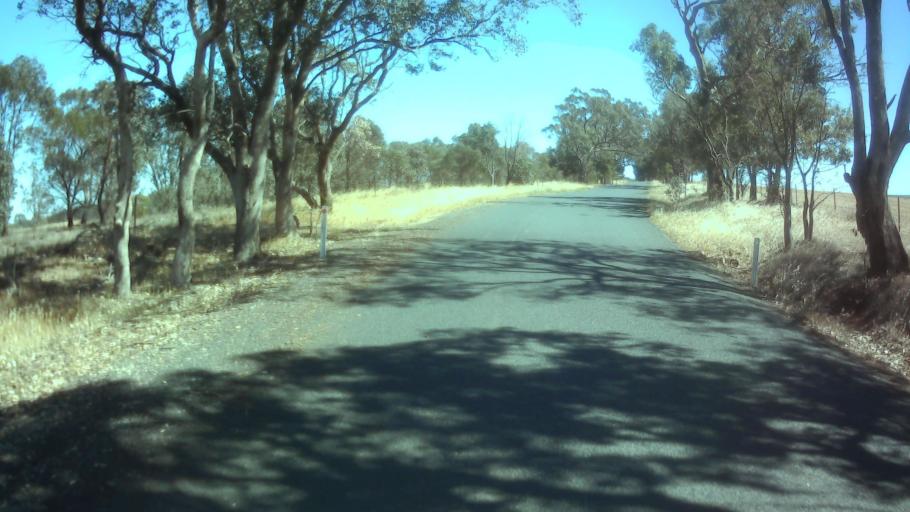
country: AU
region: New South Wales
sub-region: Weddin
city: Grenfell
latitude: -33.9452
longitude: 148.3886
